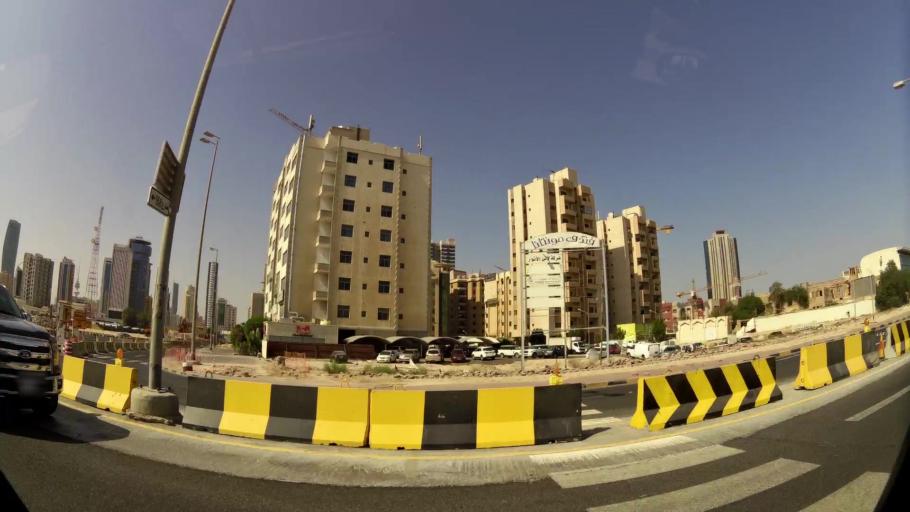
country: KW
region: Al Asimah
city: Ad Dasmah
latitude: 29.3872
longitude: 47.9952
